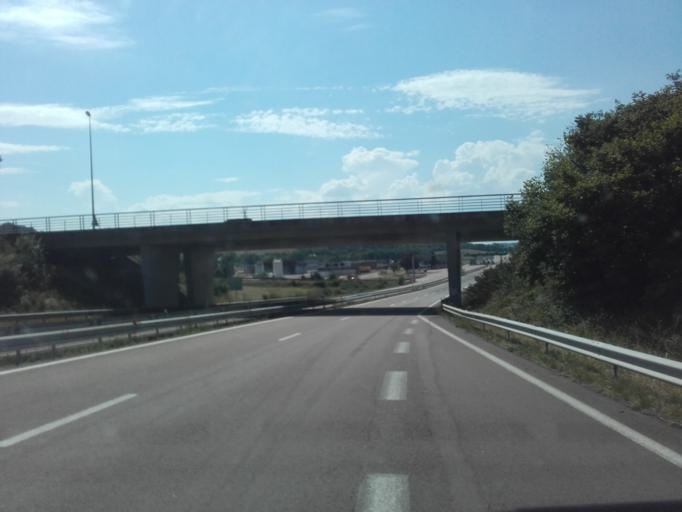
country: FR
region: Bourgogne
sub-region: Departement de la Cote-d'Or
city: Pouilly-en-Auxois
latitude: 47.2528
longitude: 4.5666
